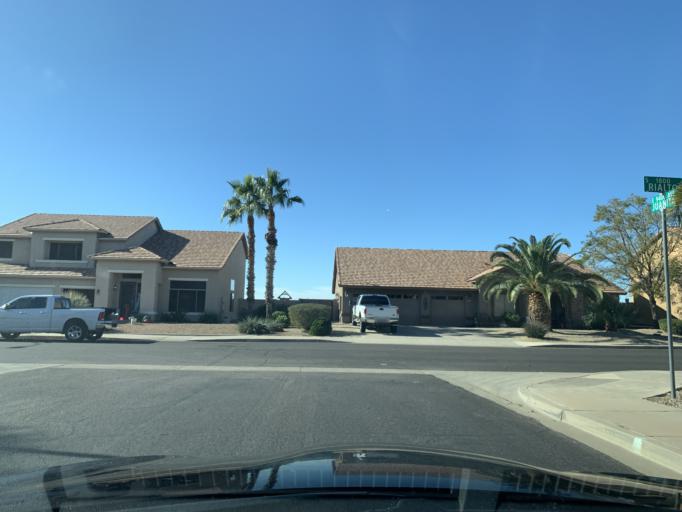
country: US
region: Arizona
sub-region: Pinal County
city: Apache Junction
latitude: 33.3819
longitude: -111.6278
